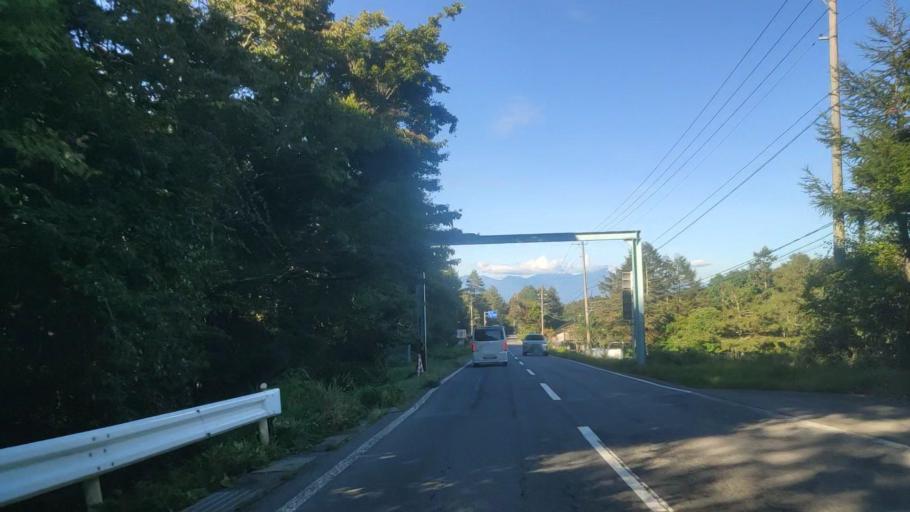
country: JP
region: Nagano
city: Kamimaruko
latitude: 36.1802
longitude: 138.2831
